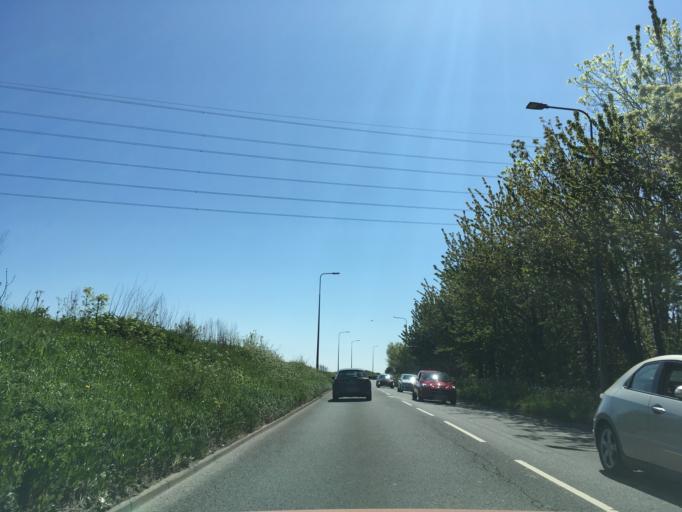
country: GB
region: Wales
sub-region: Cardiff
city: Cardiff
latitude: 51.4890
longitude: -3.1268
